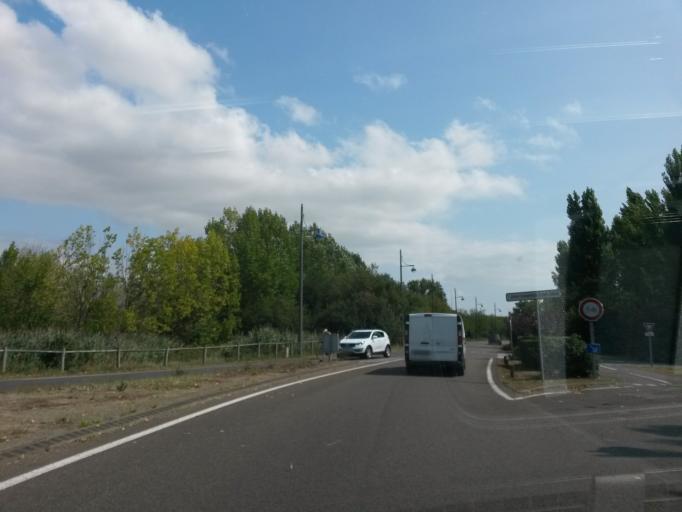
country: FR
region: Pays de la Loire
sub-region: Departement de la Vendee
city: La Tranche-sur-Mer
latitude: 46.3515
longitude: -1.4283
